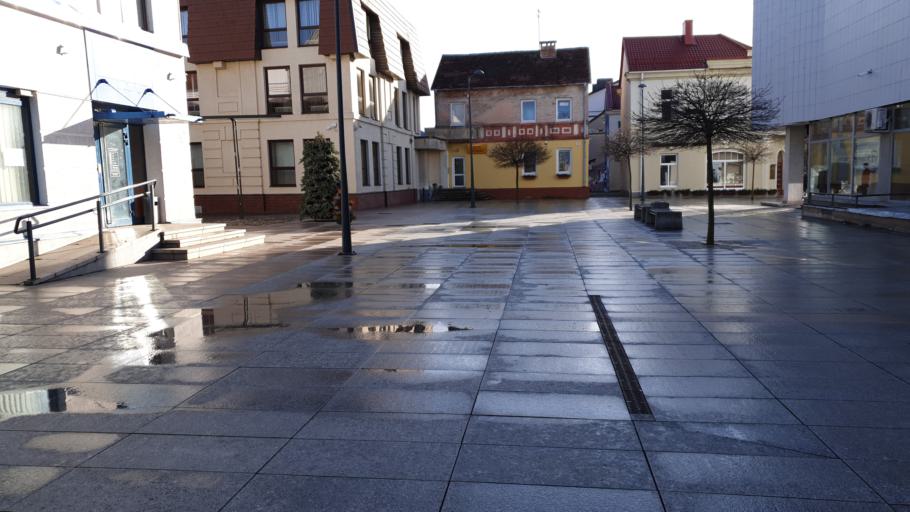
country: LT
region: Marijampoles apskritis
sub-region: Marijampole Municipality
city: Marijampole
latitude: 54.5570
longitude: 23.3510
